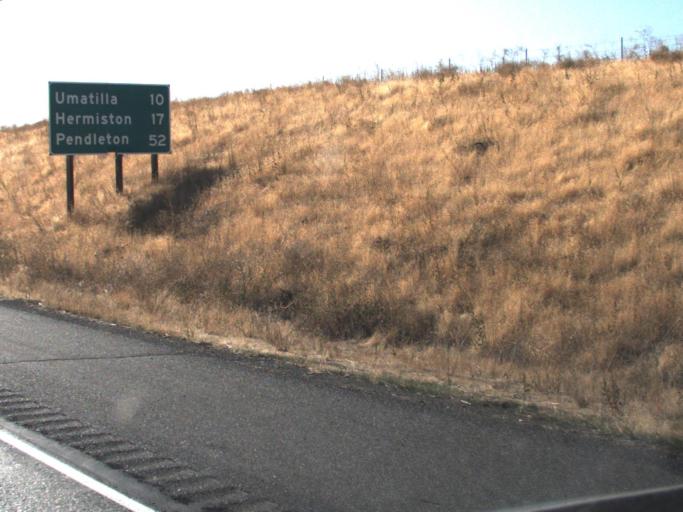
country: US
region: Oregon
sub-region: Umatilla County
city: Umatilla
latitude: 46.0124
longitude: -119.2323
